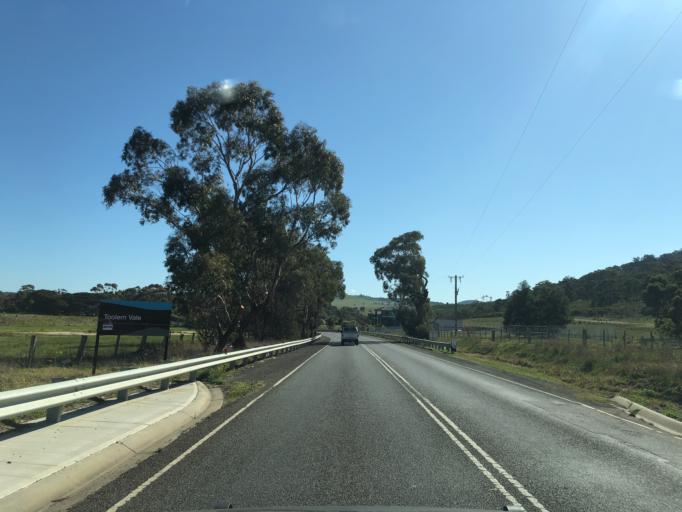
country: AU
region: Victoria
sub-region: Melton
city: Kurunjang
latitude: -37.6085
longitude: 144.6015
